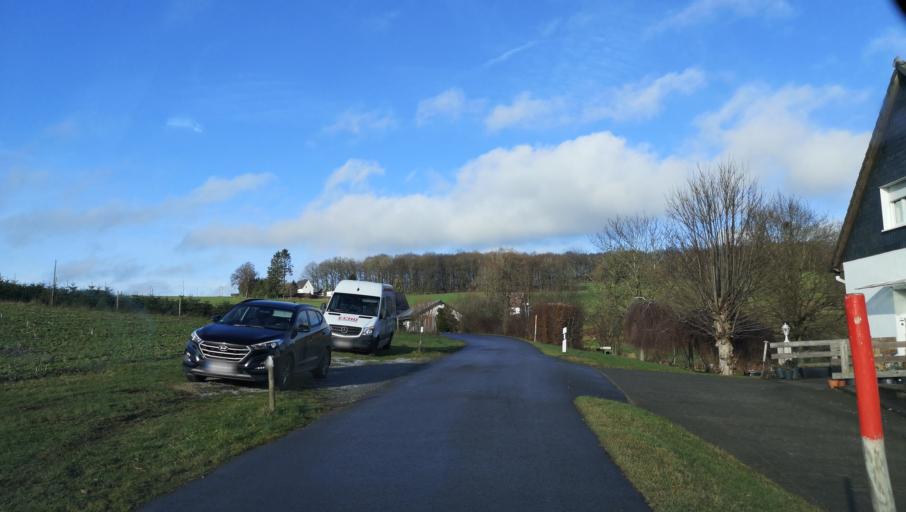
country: DE
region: North Rhine-Westphalia
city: Radevormwald
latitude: 51.1859
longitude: 7.4151
